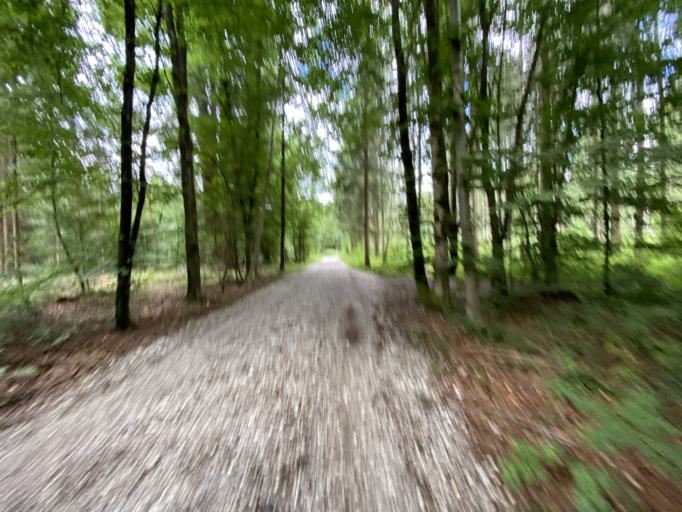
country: DE
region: Bavaria
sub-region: Upper Bavaria
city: Grafelfing
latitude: 48.1219
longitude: 11.4123
